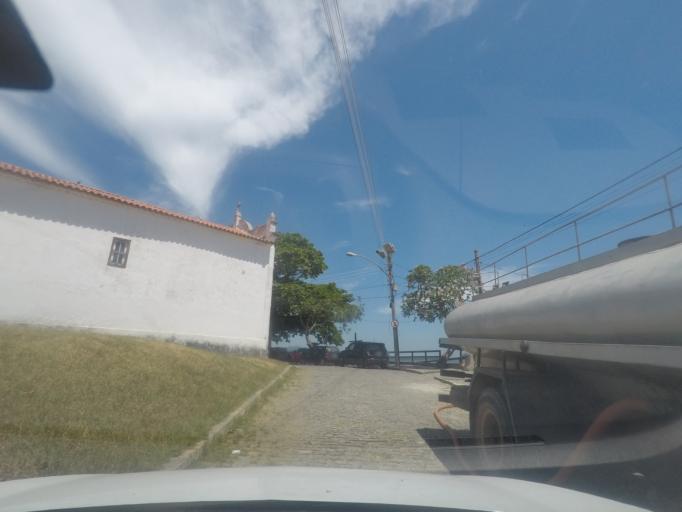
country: BR
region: Rio de Janeiro
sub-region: Itaguai
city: Itaguai
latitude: -23.0059
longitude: -43.6346
